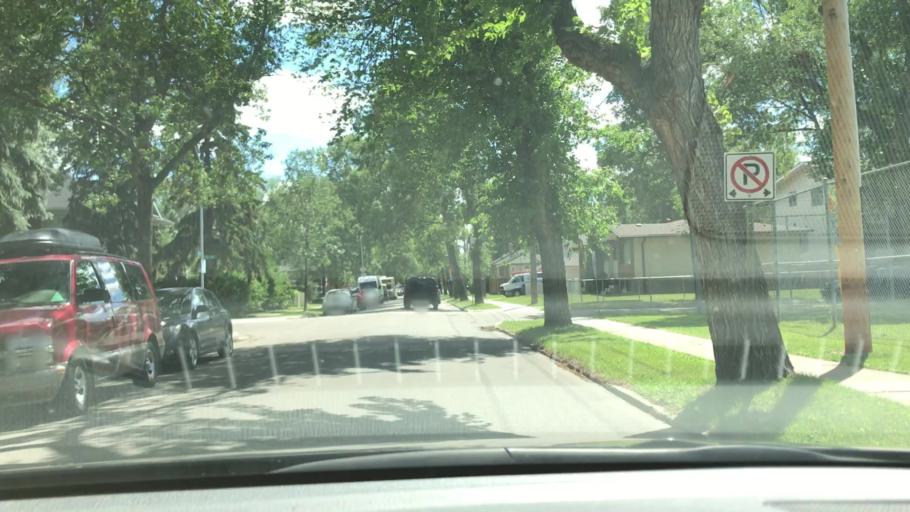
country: CA
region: Alberta
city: Edmonton
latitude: 53.5213
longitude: -113.4887
